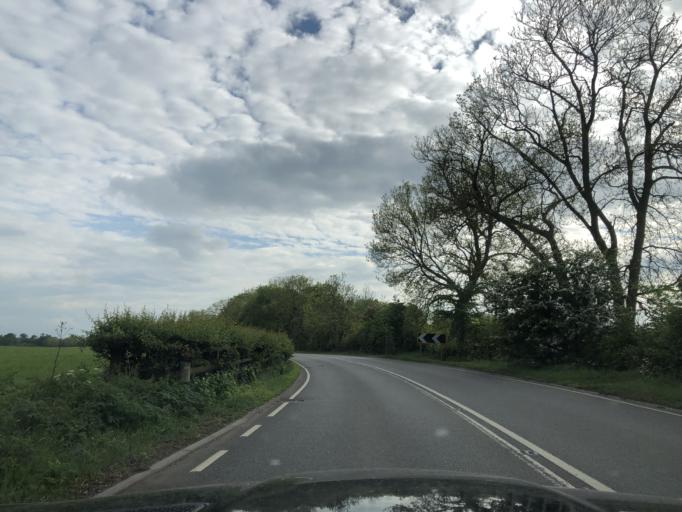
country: GB
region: England
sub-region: Warwickshire
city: Wellesbourne Mountford
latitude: 52.1775
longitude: -1.6002
